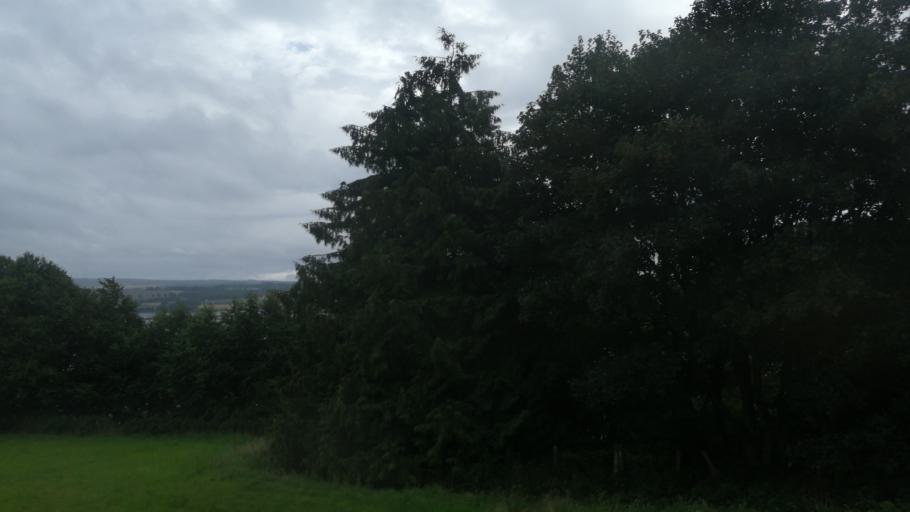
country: GB
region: Scotland
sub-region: Highland
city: Dingwall
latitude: 57.6247
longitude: -4.3801
